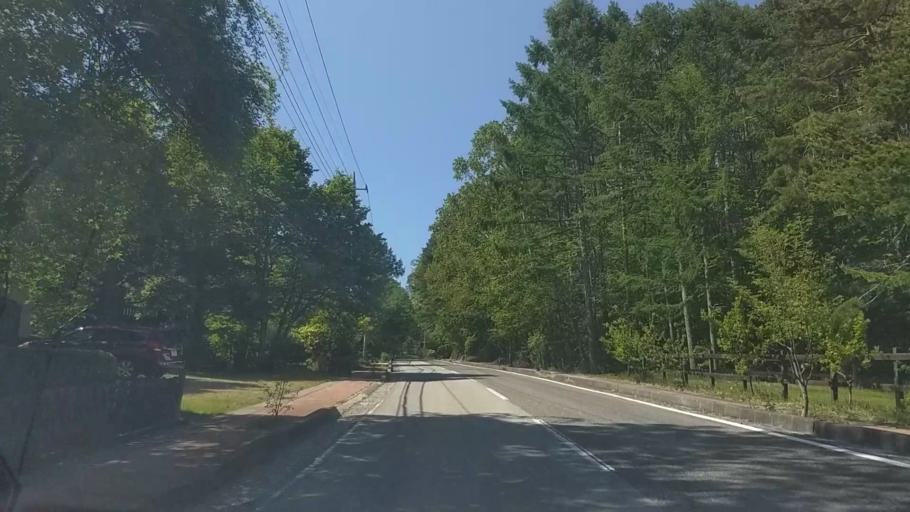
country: JP
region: Yamanashi
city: Nirasaki
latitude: 35.9001
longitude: 138.4364
